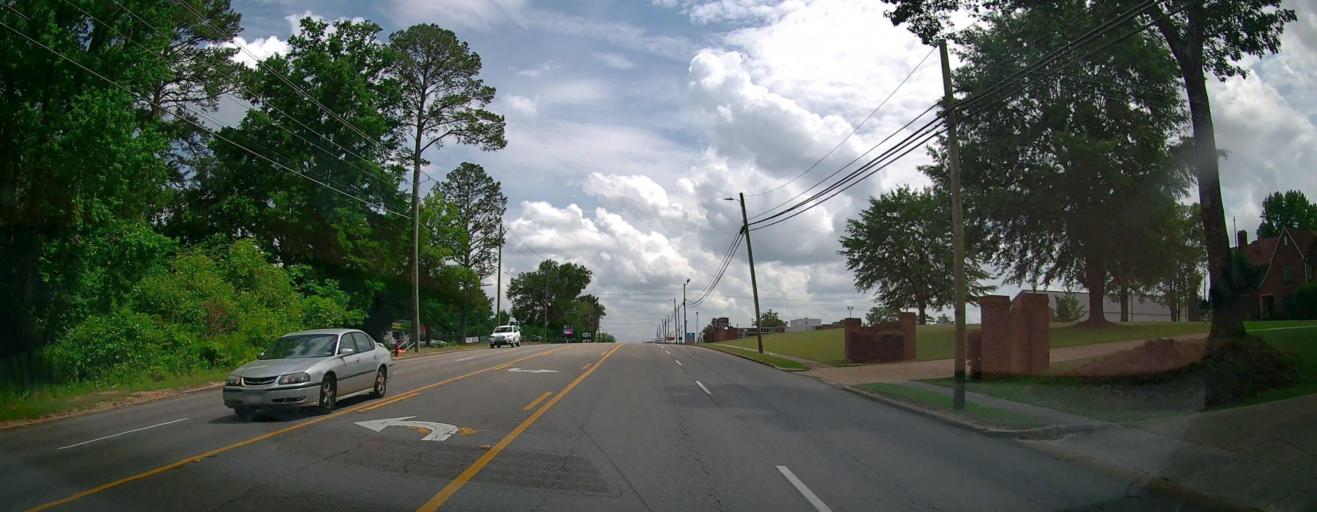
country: US
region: Alabama
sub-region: Marion County
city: Hamilton
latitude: 34.1290
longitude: -87.9899
